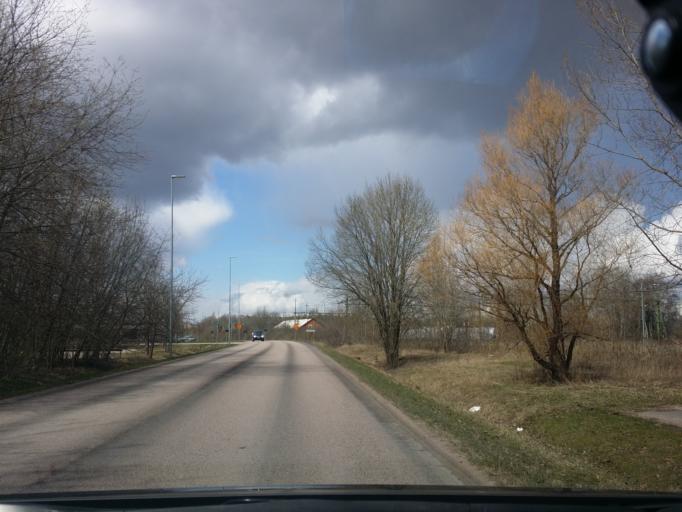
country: SE
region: Vaestmanland
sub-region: Sala Kommun
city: Sala
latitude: 59.9256
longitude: 16.6030
